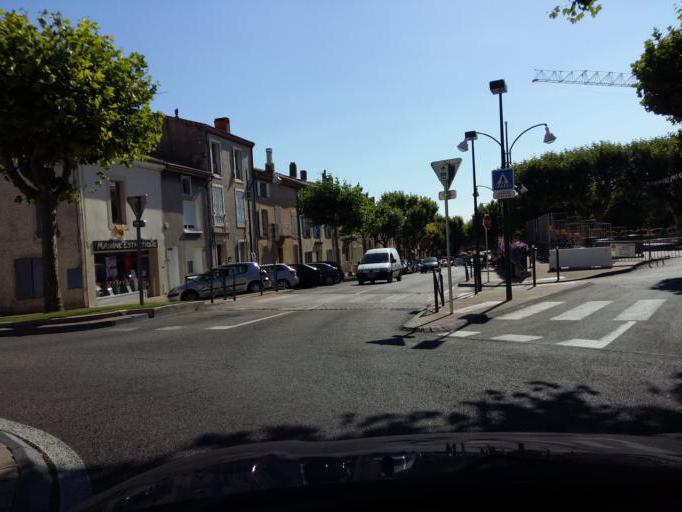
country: FR
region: Provence-Alpes-Cote d'Azur
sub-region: Departement du Vaucluse
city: Valreas
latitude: 44.3827
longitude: 4.9932
